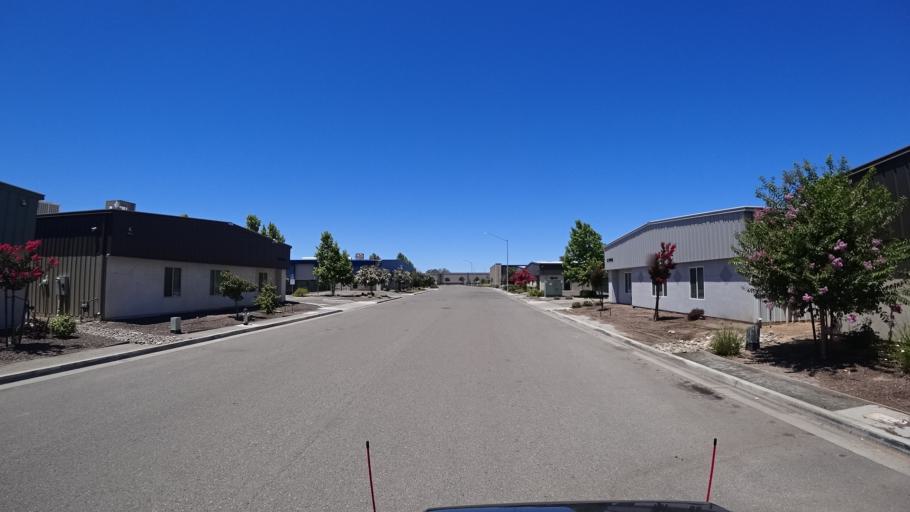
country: US
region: California
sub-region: Fresno County
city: West Park
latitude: 36.7986
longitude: -119.8602
